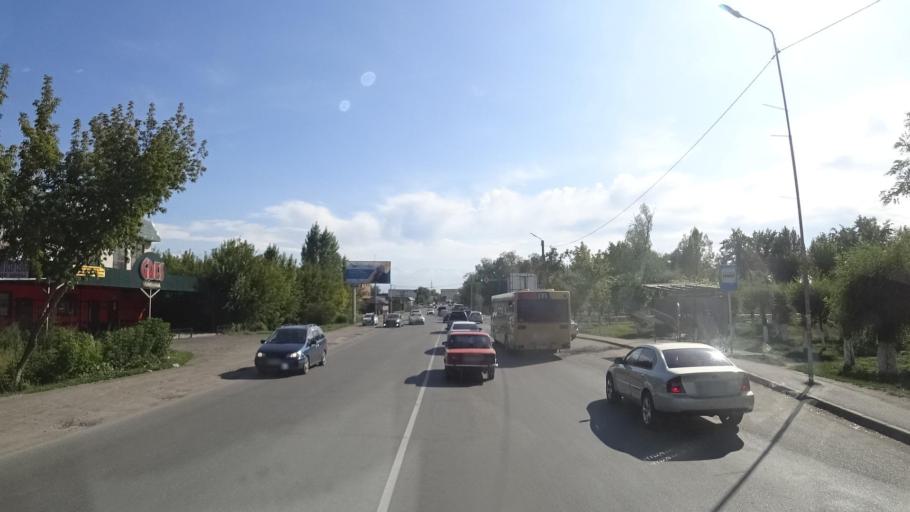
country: KZ
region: Almaty Oblysy
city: Energeticheskiy
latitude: 43.4145
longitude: 77.0203
